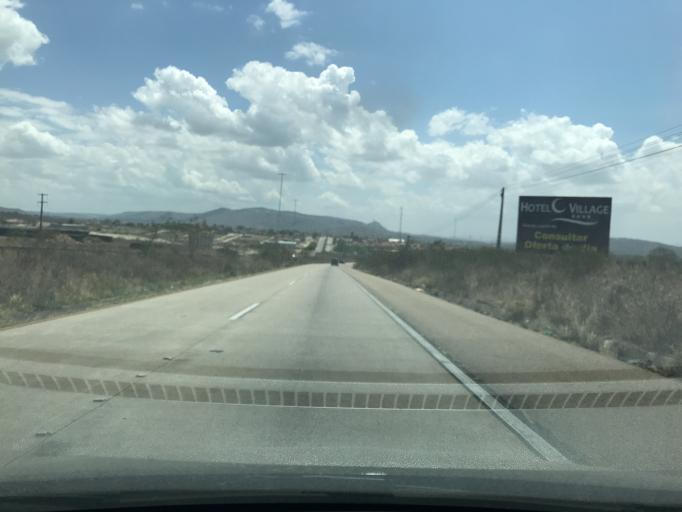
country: BR
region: Pernambuco
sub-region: Bezerros
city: Bezerros
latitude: -8.2977
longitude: -35.8335
